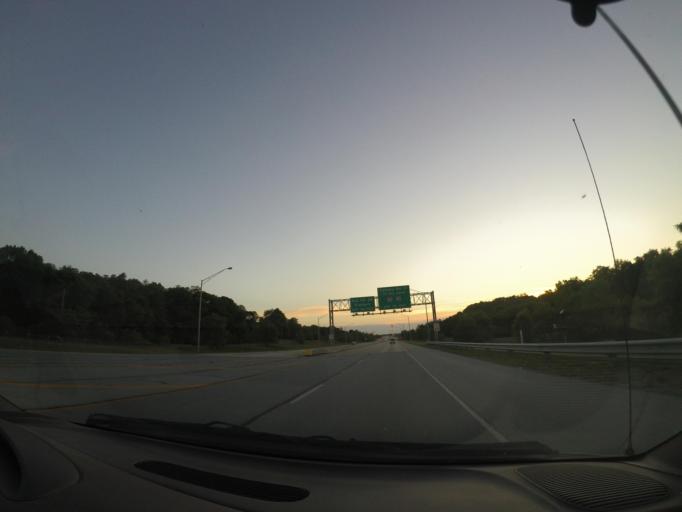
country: US
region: Indiana
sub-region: Elkhart County
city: Dunlap
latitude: 41.6671
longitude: -85.8722
